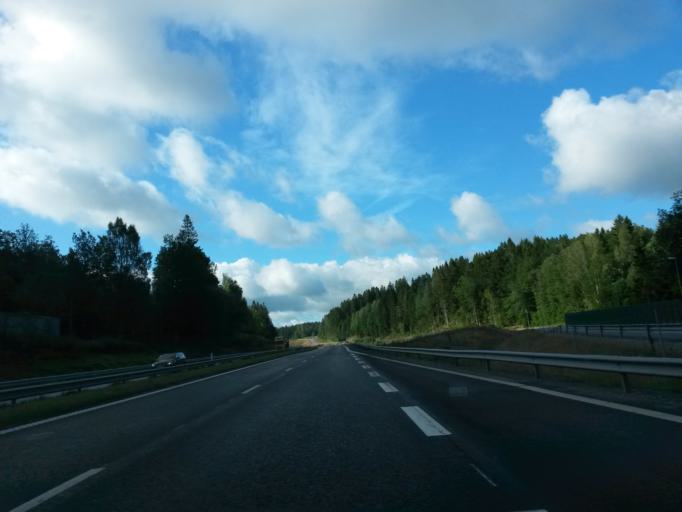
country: SE
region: Vaestra Goetaland
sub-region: Alingsas Kommun
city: Ingared
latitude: 57.8930
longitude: 12.4883
